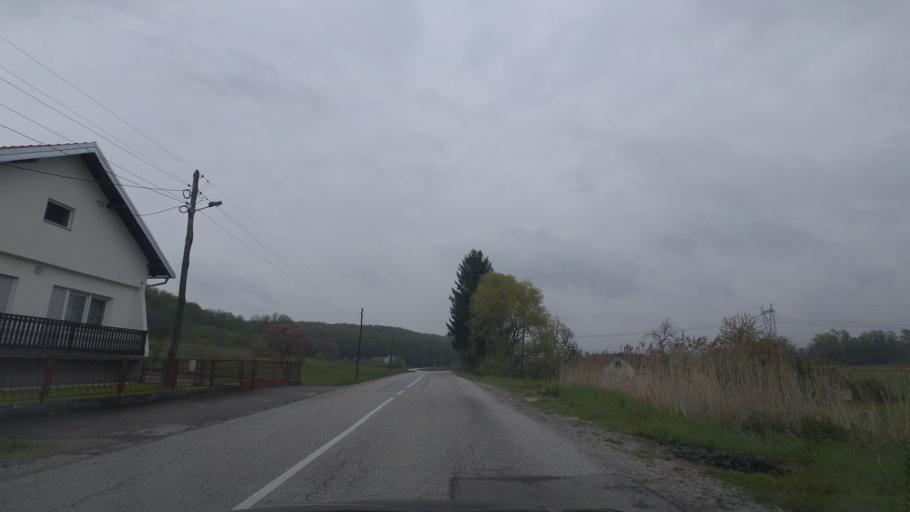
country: HR
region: Zagrebacka
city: Jastrebarsko
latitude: 45.6218
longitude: 15.5627
